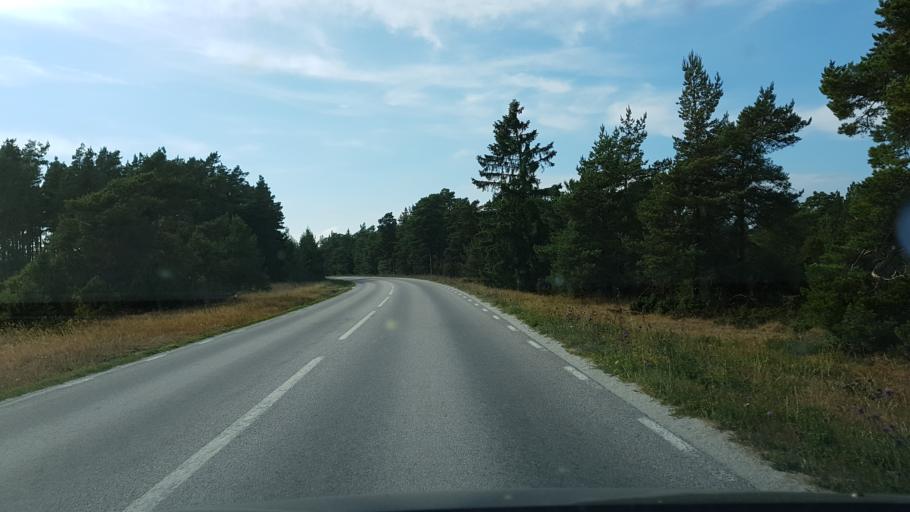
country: SE
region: Gotland
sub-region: Gotland
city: Visby
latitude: 57.6364
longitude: 18.4027
